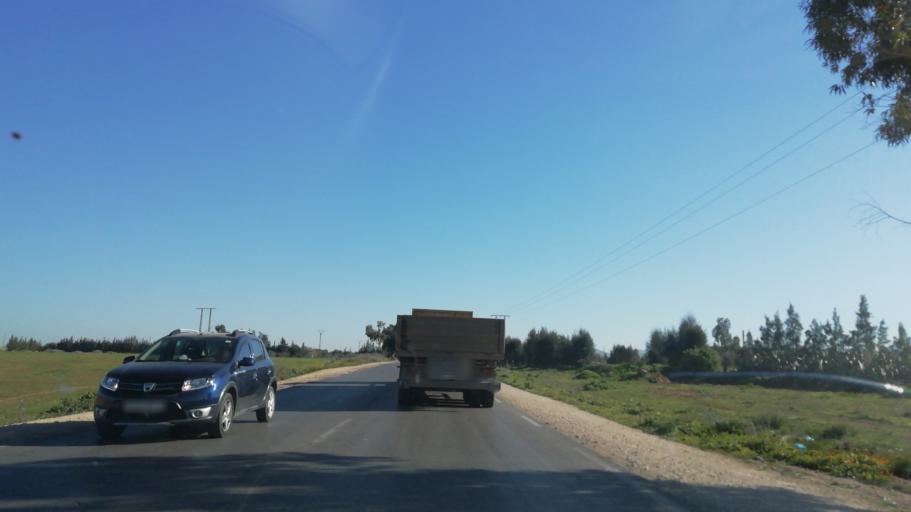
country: DZ
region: Relizane
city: Zemoura
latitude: 35.7489
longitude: 0.6915
